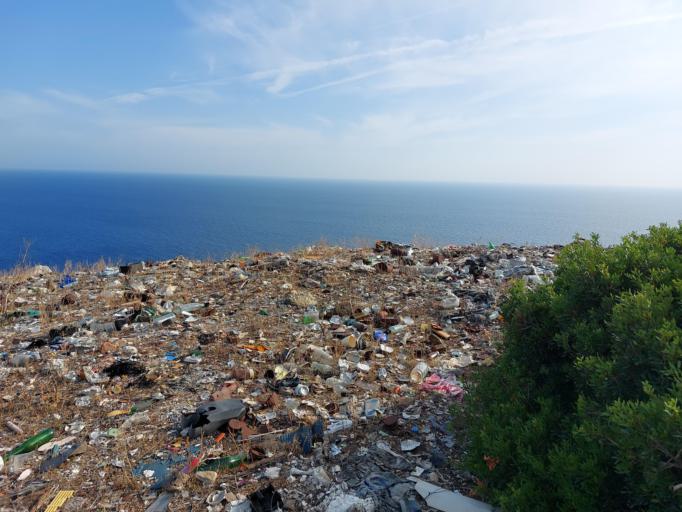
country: HR
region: Dubrovacko-Neretvanska
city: Smokvica
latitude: 42.7325
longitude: 16.8306
